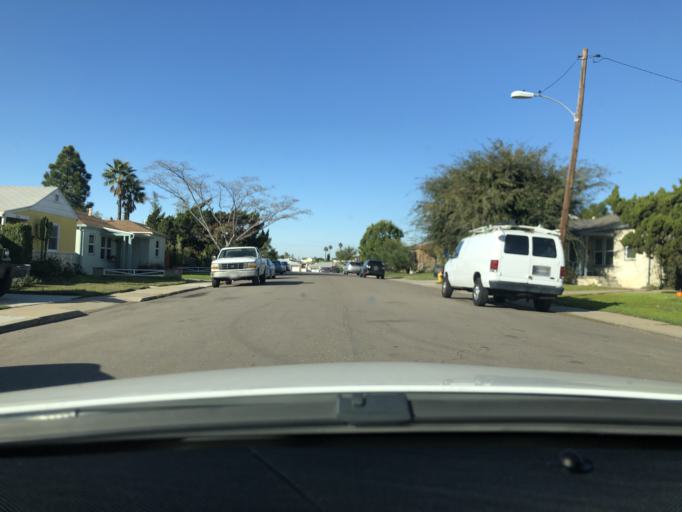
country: US
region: California
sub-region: San Diego County
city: Lemon Grove
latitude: 32.7542
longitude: -117.0704
